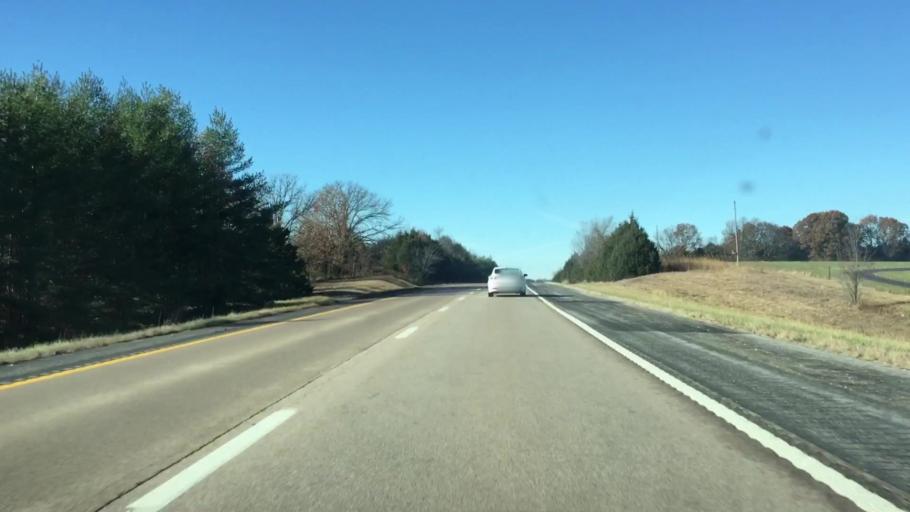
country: US
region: Missouri
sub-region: Miller County
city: Eldon
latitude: 38.3683
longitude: -92.4737
